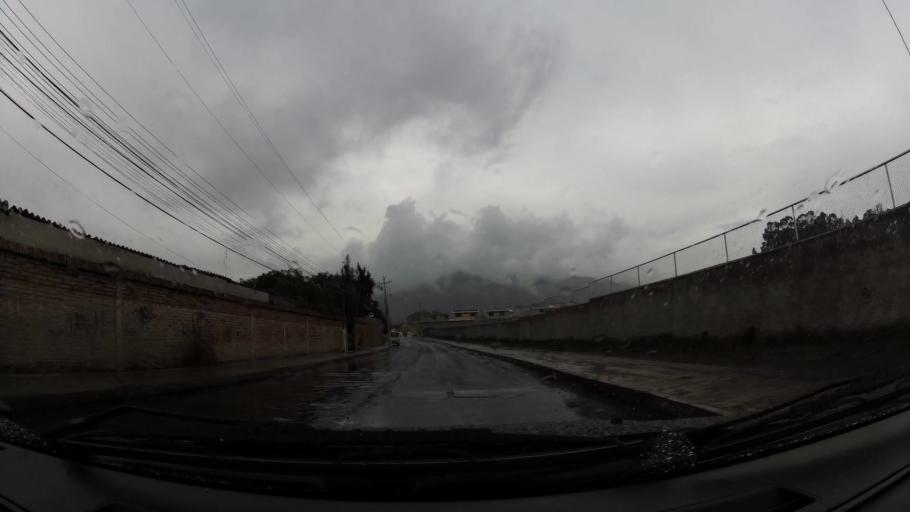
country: EC
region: Pichincha
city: Sangolqui
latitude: -0.3020
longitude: -78.4486
